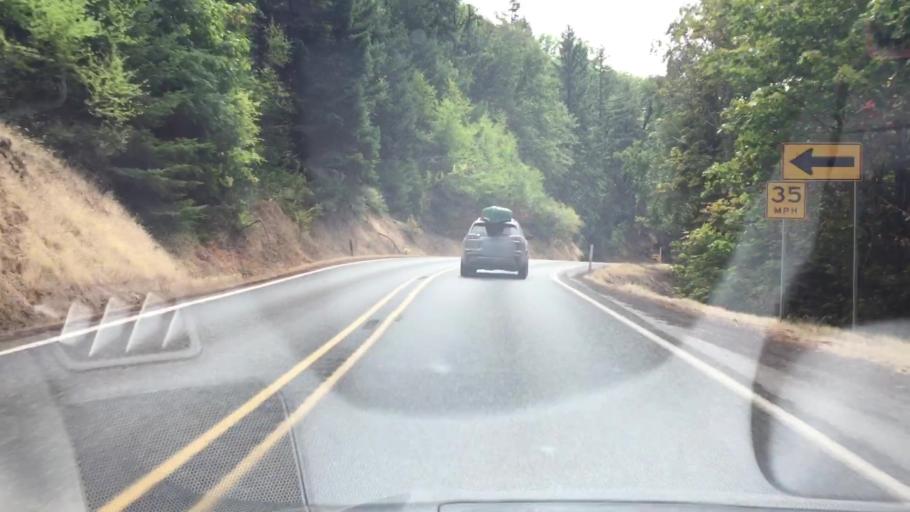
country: US
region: Washington
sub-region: Klickitat County
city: White Salmon
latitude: 45.7474
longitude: -121.5195
